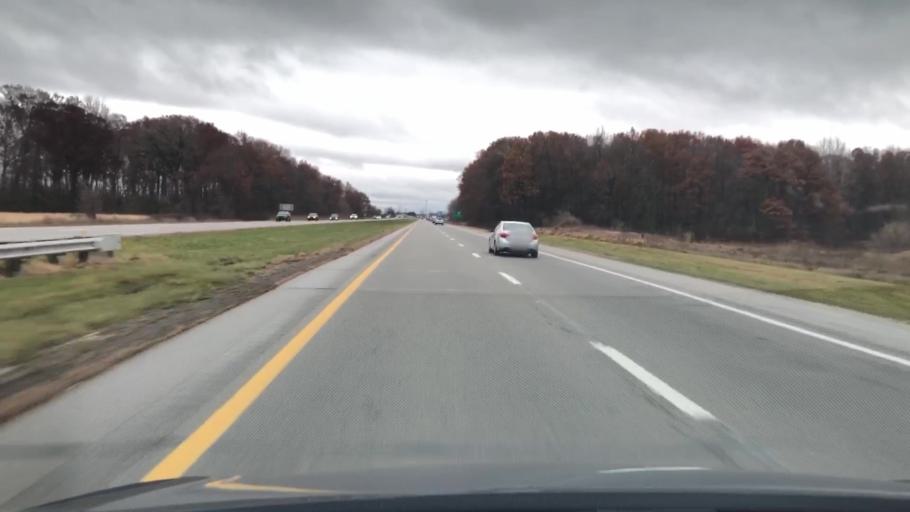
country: US
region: Ohio
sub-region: Wood County
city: Walbridge
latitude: 41.5728
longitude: -83.4681
